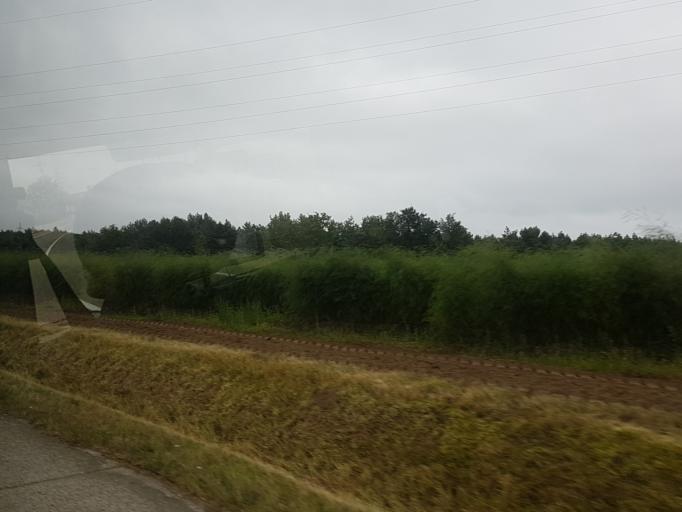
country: BE
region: Flanders
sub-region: Provincie Limburg
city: Overpelt
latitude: 51.2150
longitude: 5.3748
